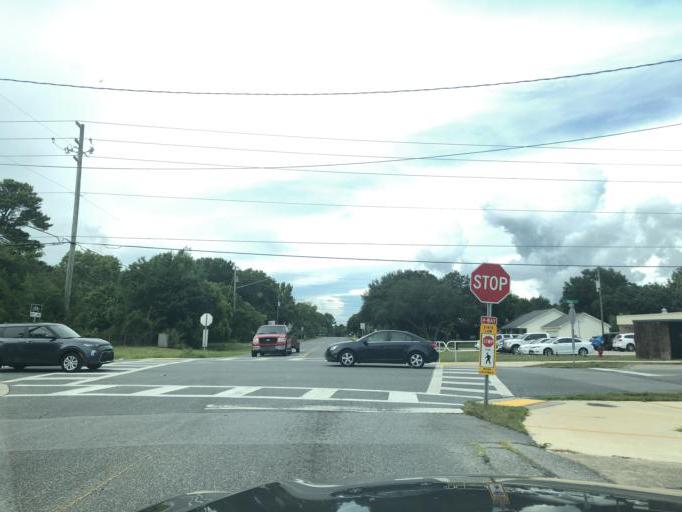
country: US
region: Florida
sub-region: Okaloosa County
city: Destin
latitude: 30.4021
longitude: -86.4952
